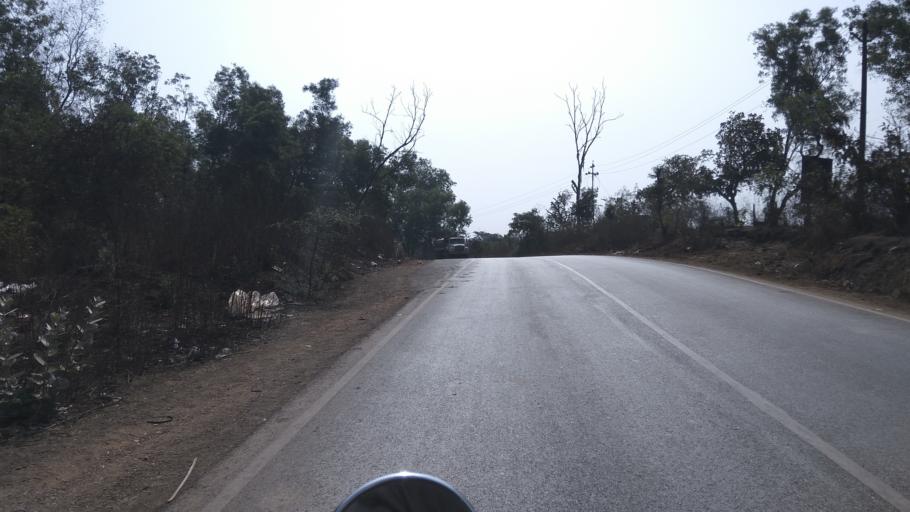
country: IN
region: Goa
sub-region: North Goa
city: Palle
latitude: 15.4156
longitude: 74.0762
